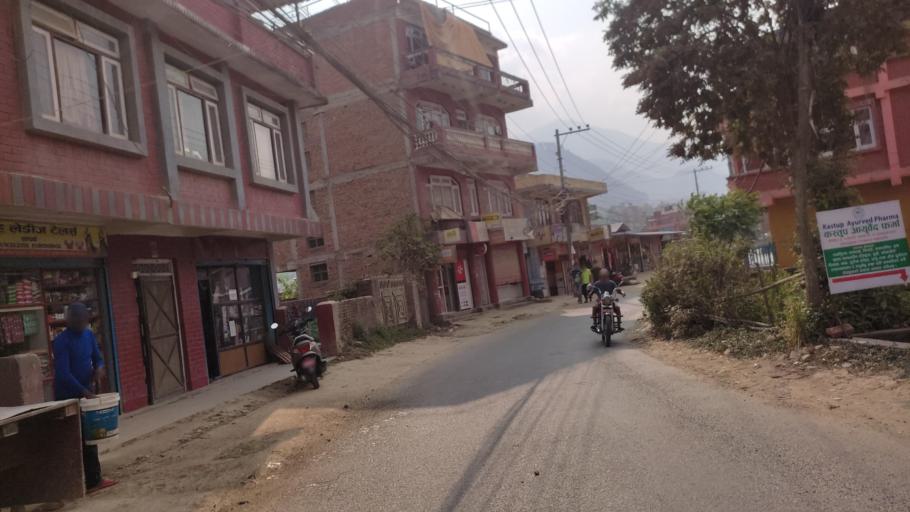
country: NP
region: Central Region
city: Kirtipur
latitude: 27.6662
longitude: 85.2641
